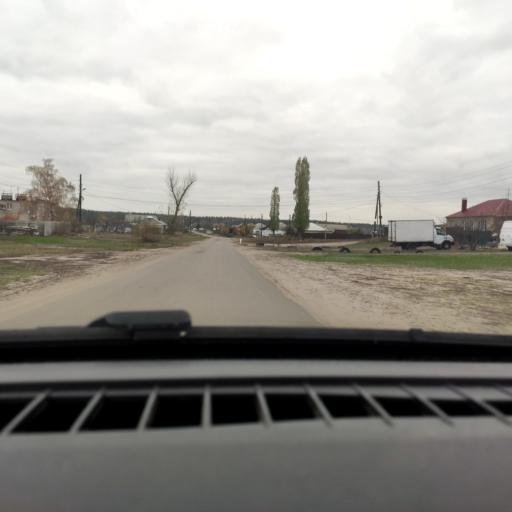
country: RU
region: Voronezj
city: Maslovka
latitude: 51.5796
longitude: 39.3027
